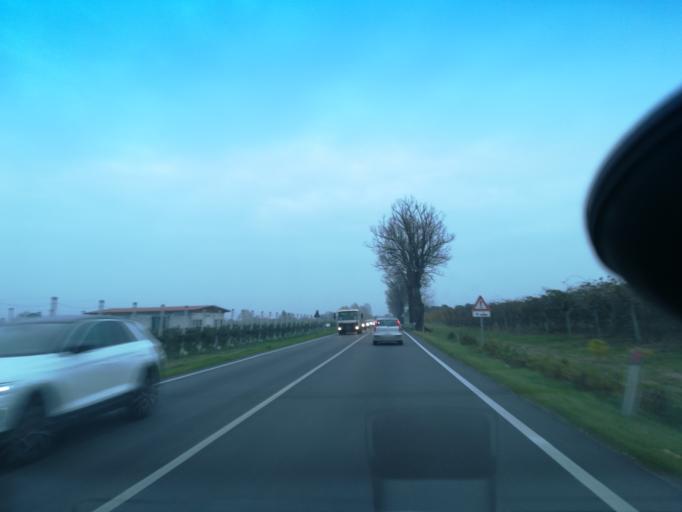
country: IT
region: Emilia-Romagna
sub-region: Provincia di Ravenna
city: Castel Bolognese
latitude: 44.3161
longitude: 11.8084
